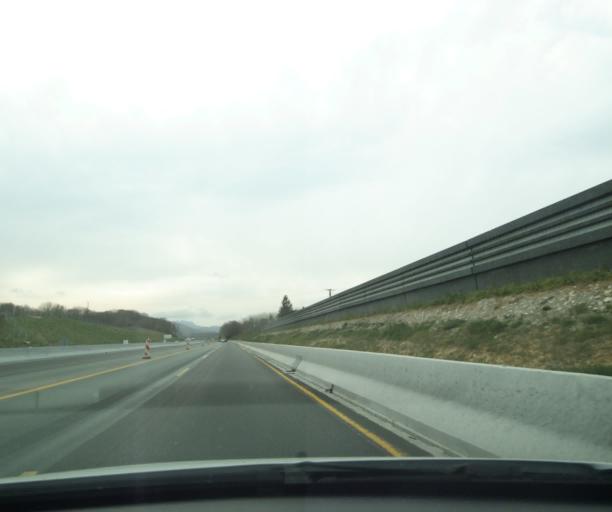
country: FR
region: Aquitaine
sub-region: Departement des Pyrenees-Atlantiques
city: Ciboure
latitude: 43.3688
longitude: -1.6831
